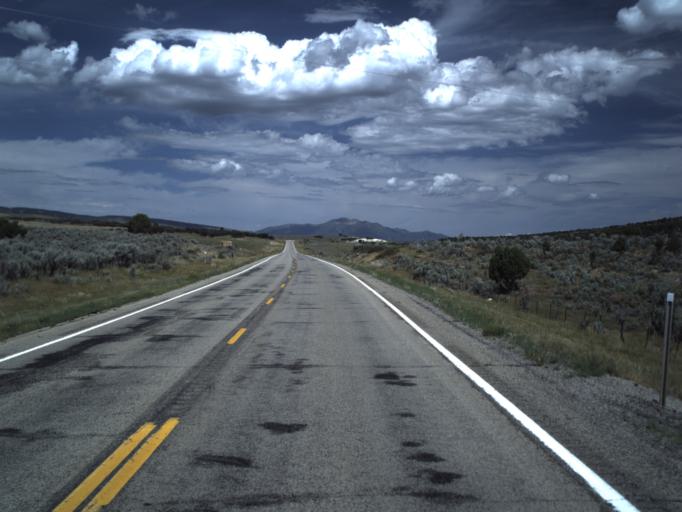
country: US
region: Utah
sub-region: Sanpete County
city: Fairview
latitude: 39.6938
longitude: -111.4615
